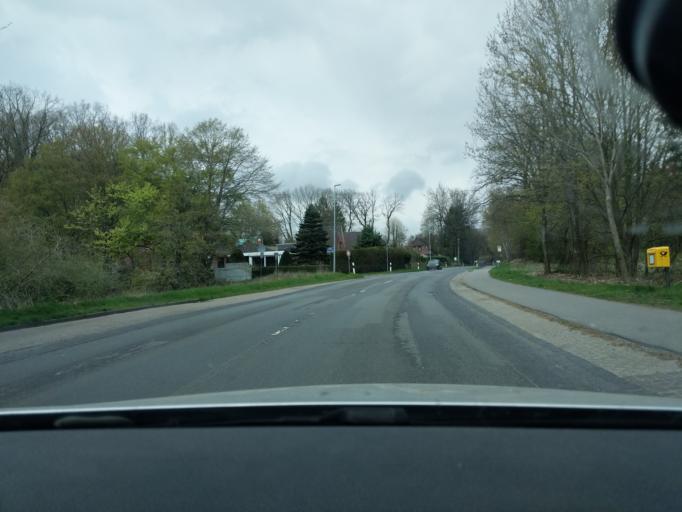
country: DE
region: Lower Saxony
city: Stade
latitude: 53.5757
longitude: 9.4700
